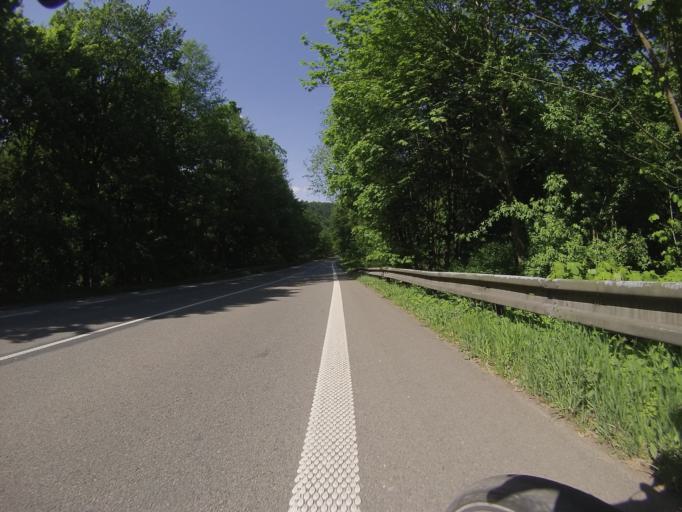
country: CZ
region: South Moravian
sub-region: Okres Blansko
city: Adamov
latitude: 49.3279
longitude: 16.6433
